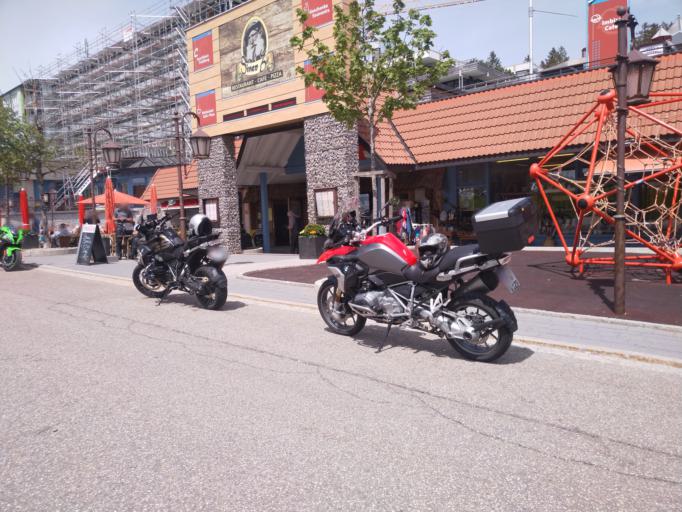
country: DE
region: Baden-Wuerttemberg
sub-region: Freiburg Region
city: Bernau
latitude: 47.8595
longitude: 8.0368
